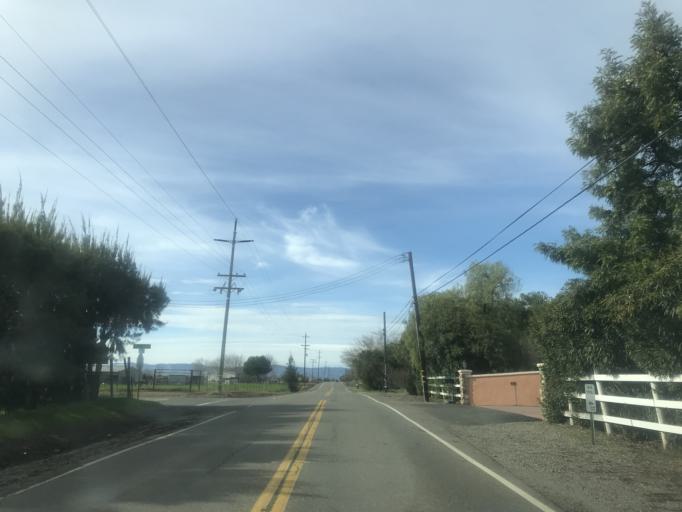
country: US
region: California
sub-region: Yolo County
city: Woodland
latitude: 38.6635
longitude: -121.8692
